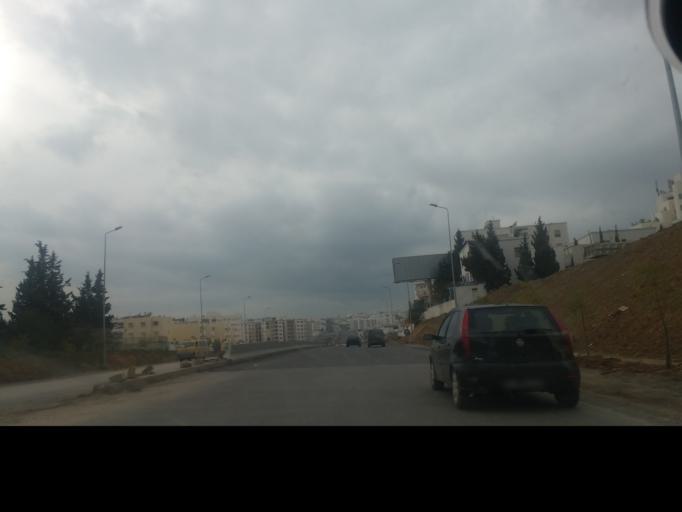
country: TN
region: Ariana
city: Ariana
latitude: 36.8550
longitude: 10.1572
